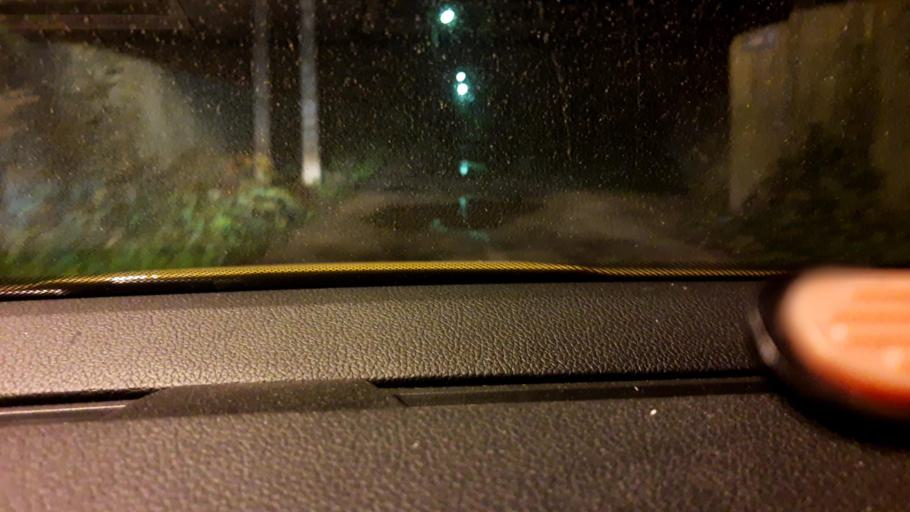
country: RU
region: Moskovskaya
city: Kratovo
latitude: 55.5696
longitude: 38.1826
